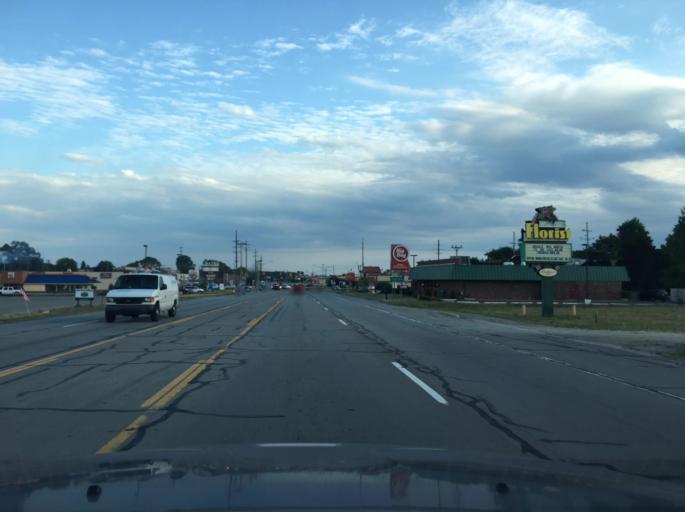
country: US
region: Michigan
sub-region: Macomb County
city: Mount Clemens
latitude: 42.6010
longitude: -82.8996
